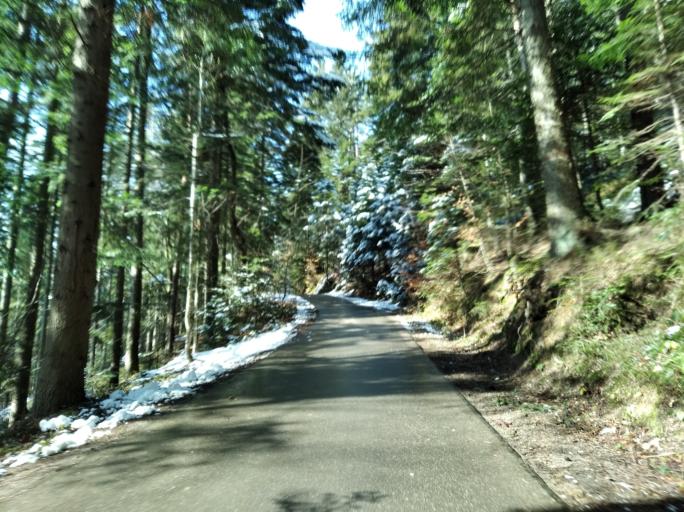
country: PL
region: Subcarpathian Voivodeship
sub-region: Powiat krosnienski
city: Korczyna
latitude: 49.7433
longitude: 21.8234
